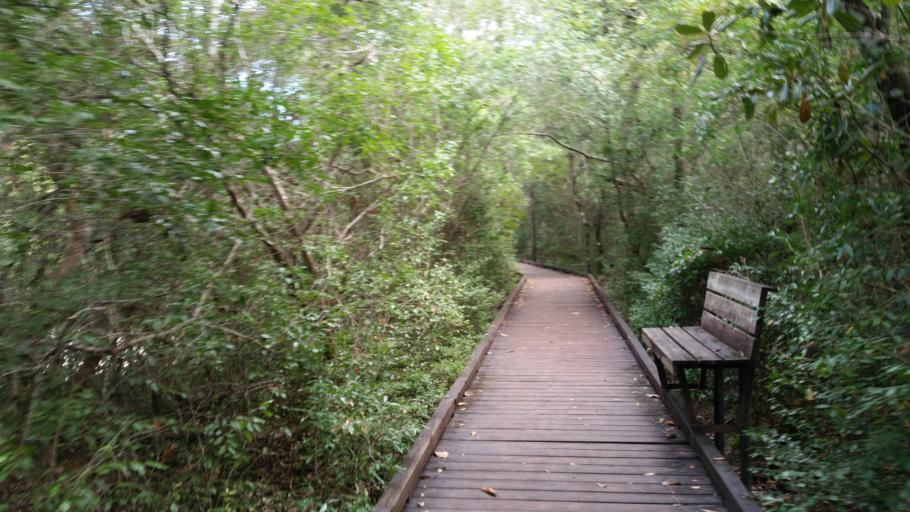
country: US
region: Florida
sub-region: Santa Rosa County
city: Point Baker
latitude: 30.8614
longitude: -86.8490
